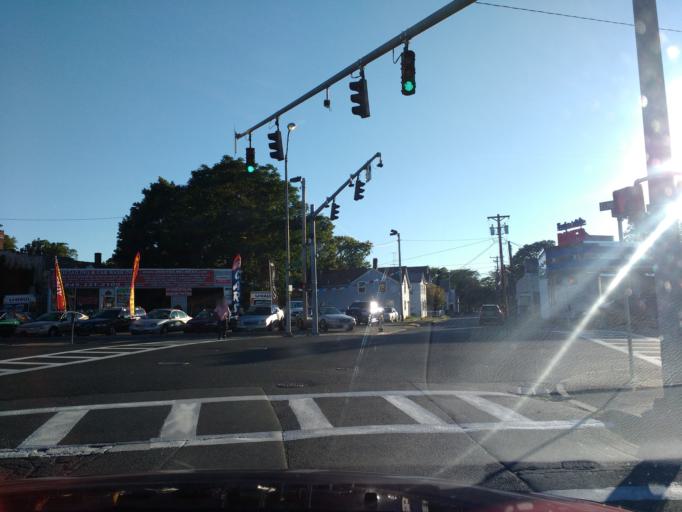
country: US
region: New York
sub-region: Ulster County
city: Kingston
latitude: 41.9313
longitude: -74.0086
